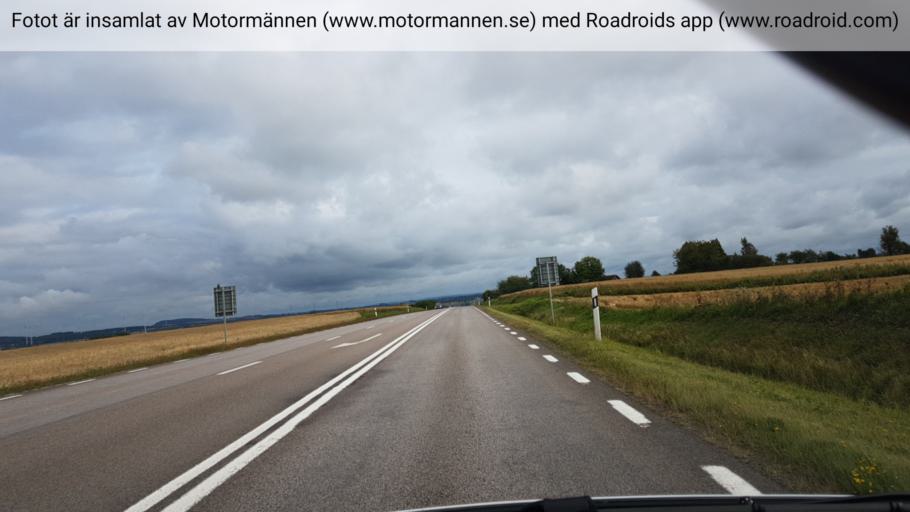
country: SE
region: Vaestra Goetaland
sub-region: Falkopings Kommun
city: Falkoeping
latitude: 58.1455
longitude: 13.6203
